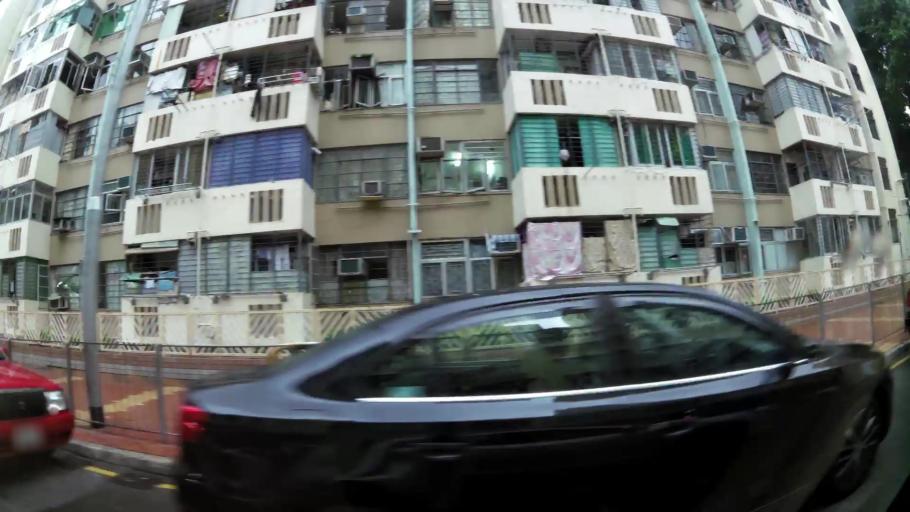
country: HK
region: Tsuen Wan
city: Tsuen Wan
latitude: 22.3727
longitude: 114.1152
